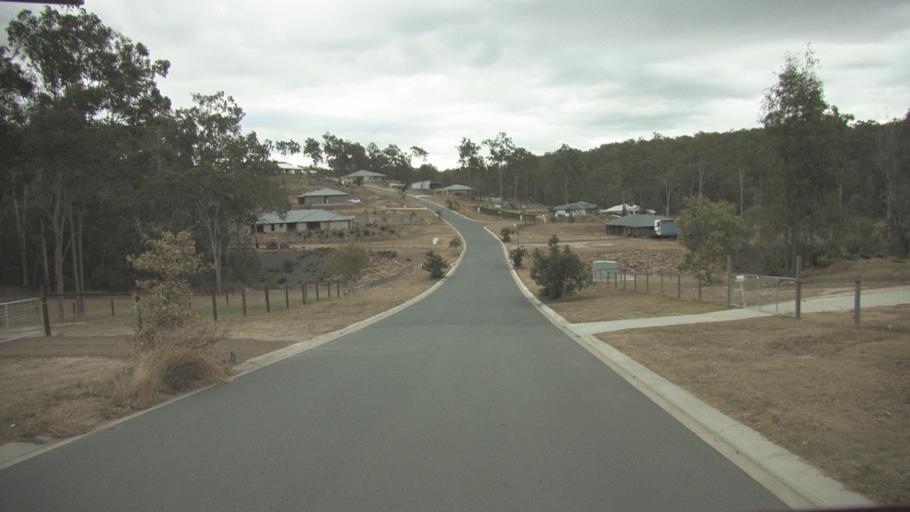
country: AU
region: Queensland
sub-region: Logan
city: Cedar Vale
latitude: -27.8618
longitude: 153.0786
